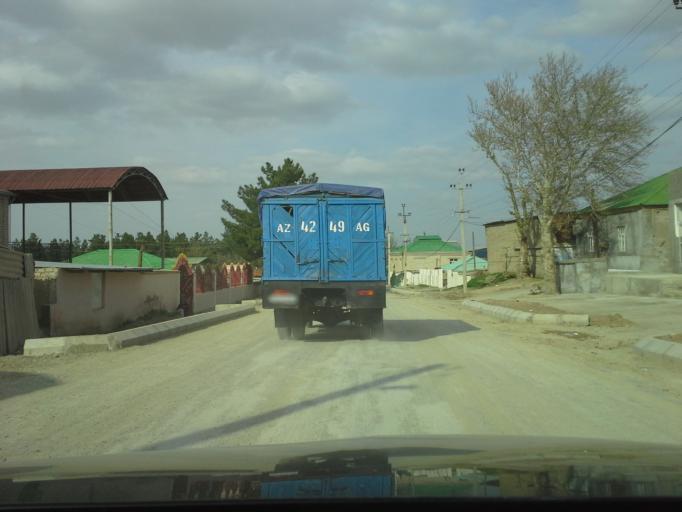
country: TM
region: Ahal
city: Abadan
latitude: 37.9580
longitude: 58.2084
